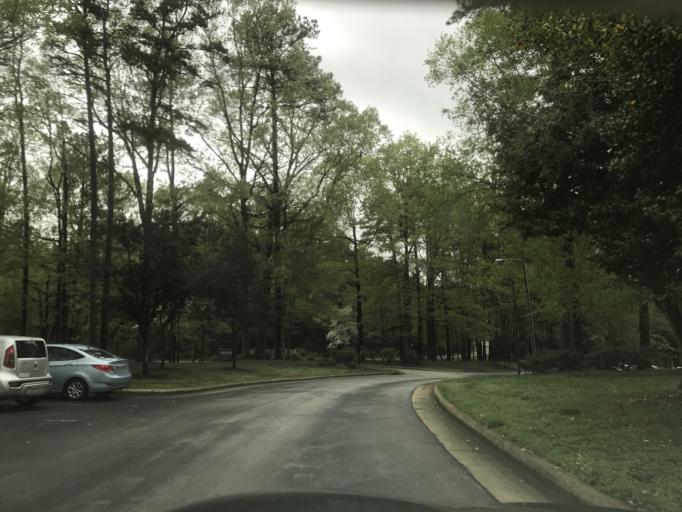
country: US
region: North Carolina
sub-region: Wake County
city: West Raleigh
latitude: 35.7588
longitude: -78.7040
